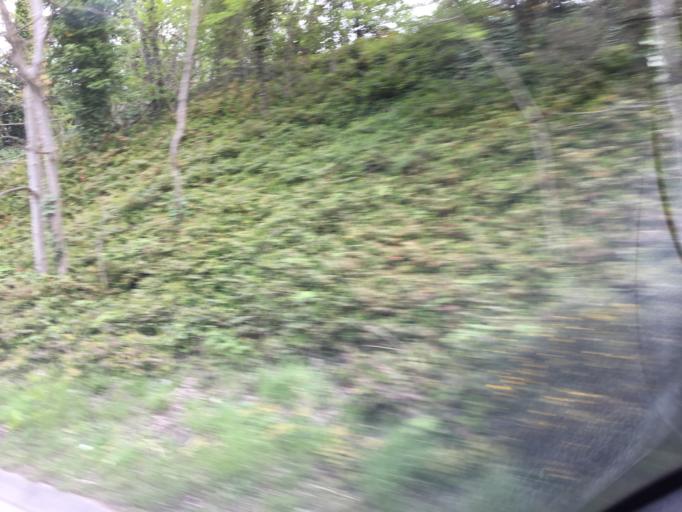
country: GB
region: England
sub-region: Bath and North East Somerset
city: Radstock
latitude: 51.2944
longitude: -2.4485
